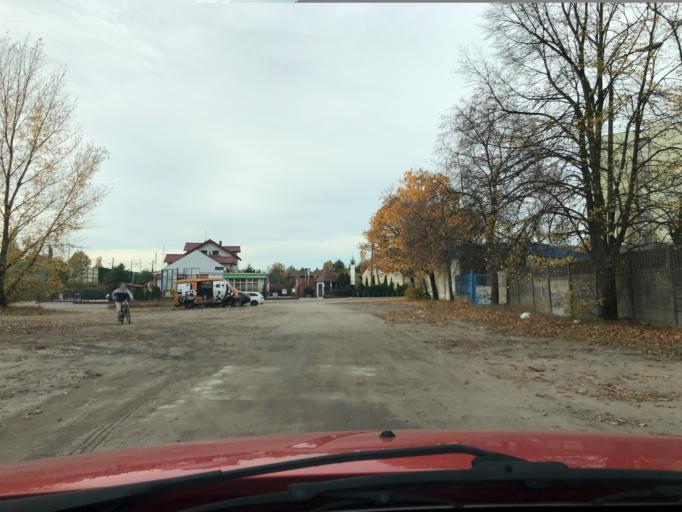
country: PL
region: Greater Poland Voivodeship
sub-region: Powiat poznanski
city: Plewiska
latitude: 52.3790
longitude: 16.8400
